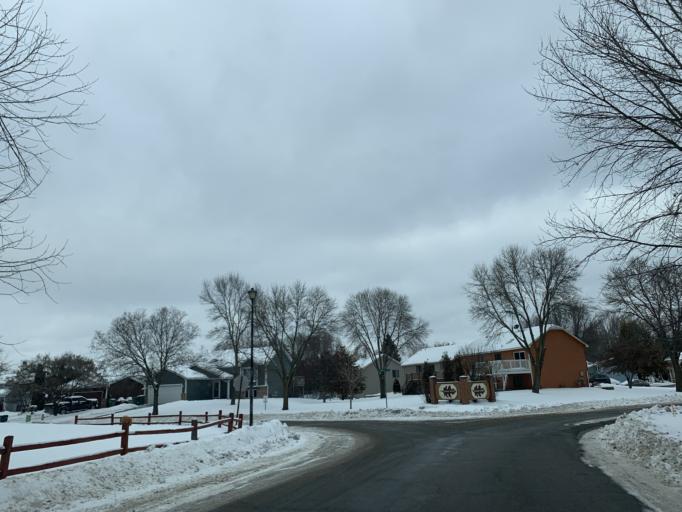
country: US
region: Minnesota
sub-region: Anoka County
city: Coon Rapids
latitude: 45.1644
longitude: -93.2818
